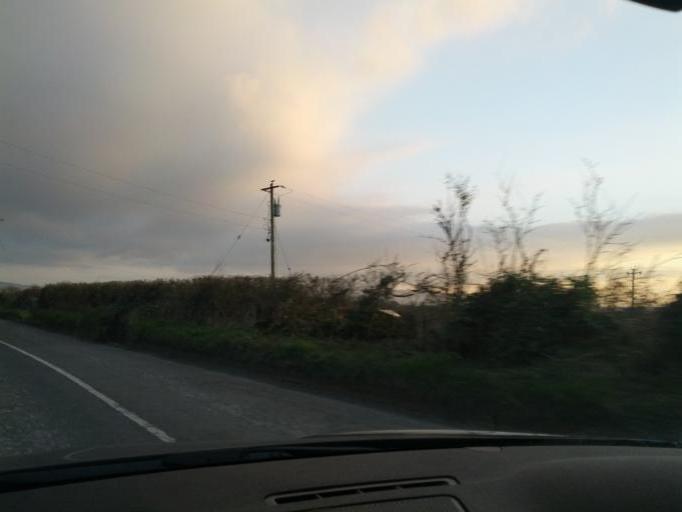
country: IE
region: Munster
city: Nenagh Bridge
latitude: 52.9034
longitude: -8.2111
